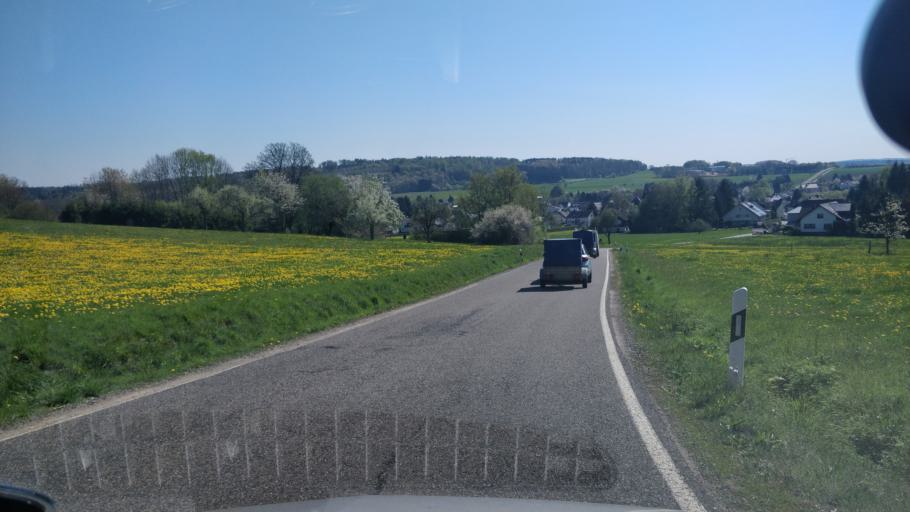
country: DE
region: Hesse
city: Waldbrunn
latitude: 50.5266
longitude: 8.0867
